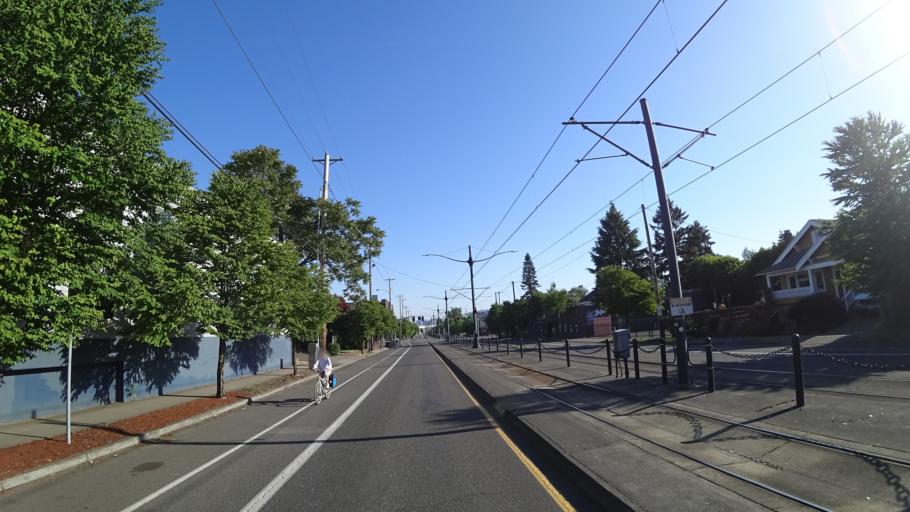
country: US
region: Oregon
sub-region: Multnomah County
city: Portland
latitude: 45.5531
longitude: -122.6809
